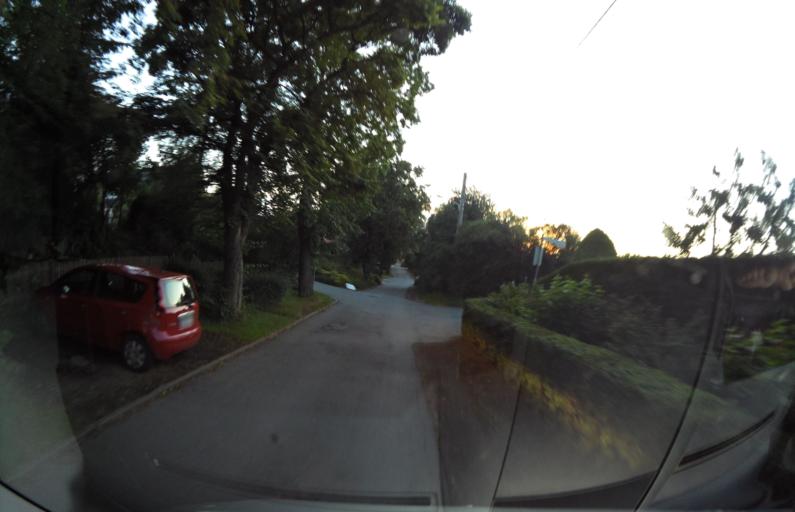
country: DE
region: Thuringia
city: Schleiz
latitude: 50.5752
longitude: 11.8198
